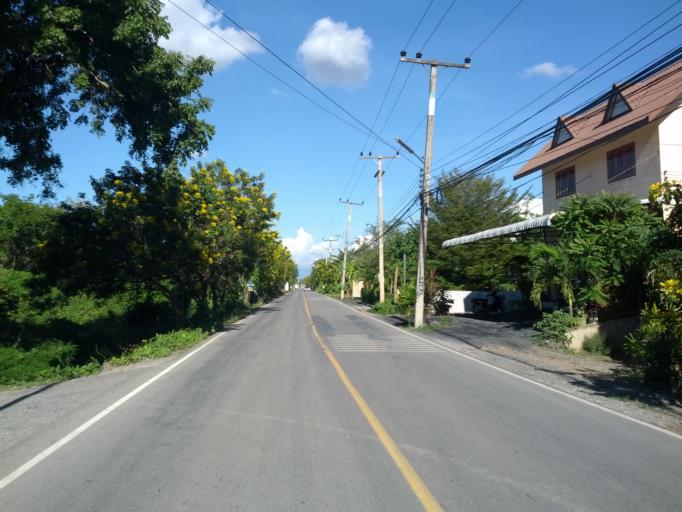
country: TH
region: Chiang Mai
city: Saraphi
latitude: 18.6916
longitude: 99.0037
